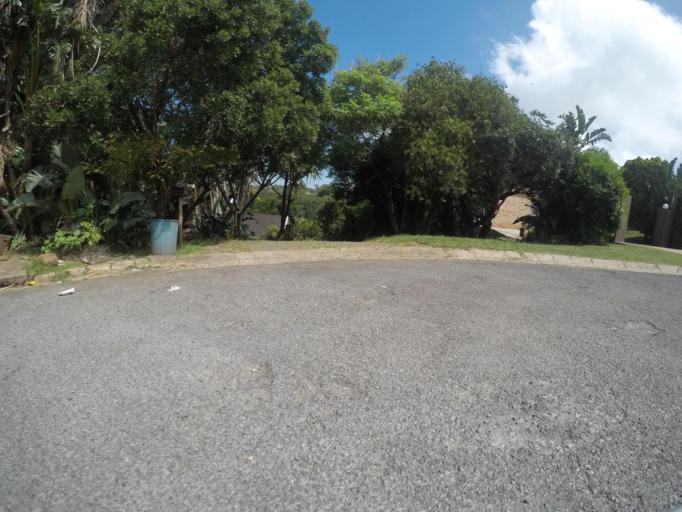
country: ZA
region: Eastern Cape
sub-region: Buffalo City Metropolitan Municipality
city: East London
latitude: -32.9715
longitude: 27.9077
